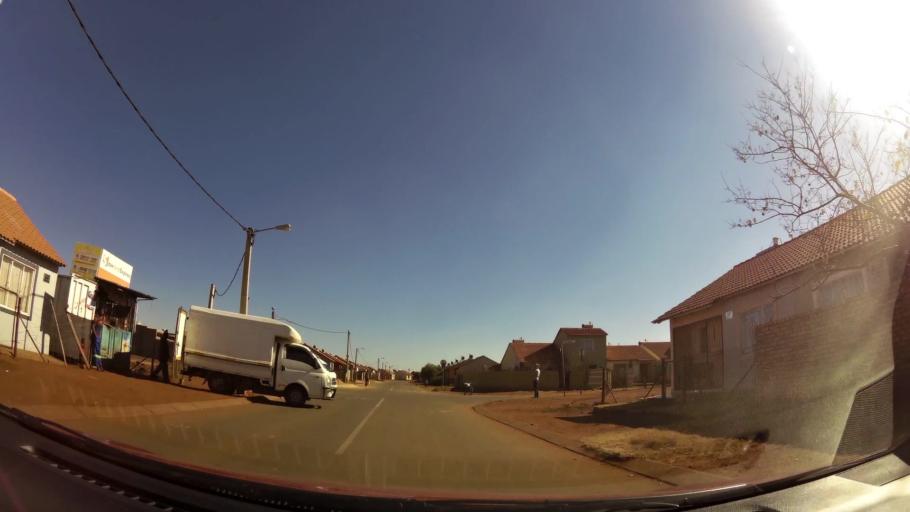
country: ZA
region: Gauteng
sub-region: City of Johannesburg Metropolitan Municipality
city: Soweto
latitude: -26.2370
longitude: 27.7996
